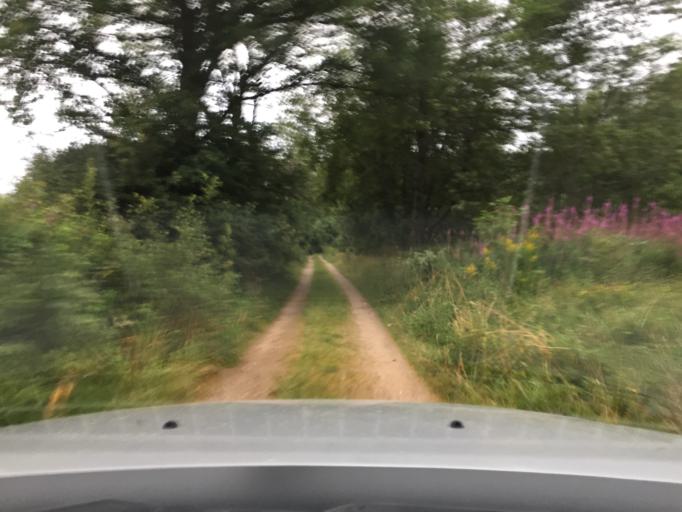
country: SE
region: Skane
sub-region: Hassleholms Kommun
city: Sosdala
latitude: 56.0402
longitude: 13.6905
